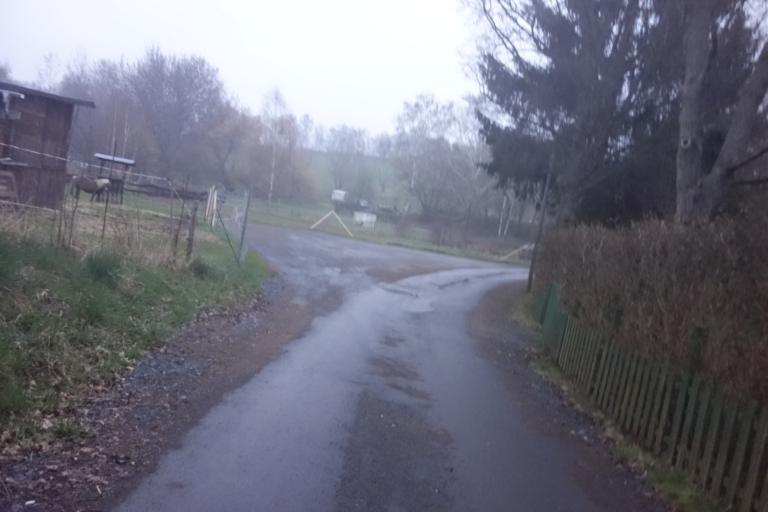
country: DE
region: Saxony
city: Freiberg
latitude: 50.8973
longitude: 13.3616
